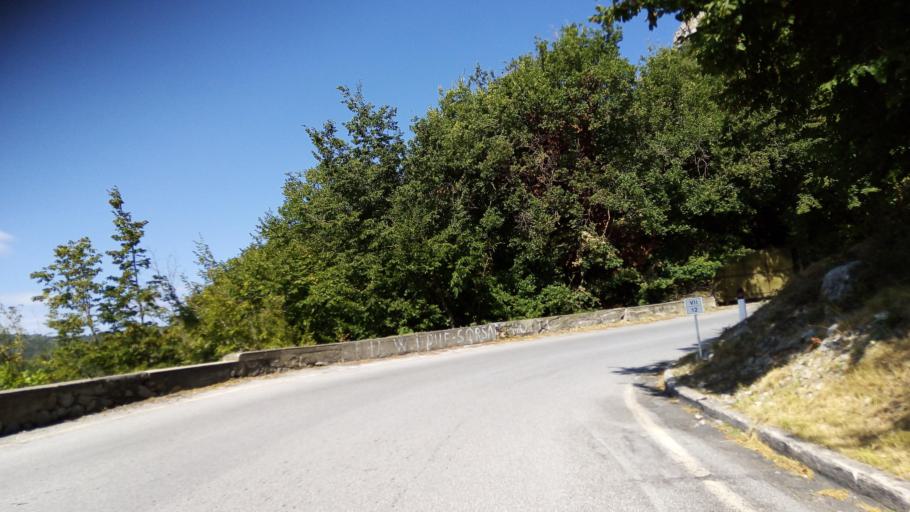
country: IT
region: Liguria
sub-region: Provincia di Savona
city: Balestrino
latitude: 44.1464
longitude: 8.1657
